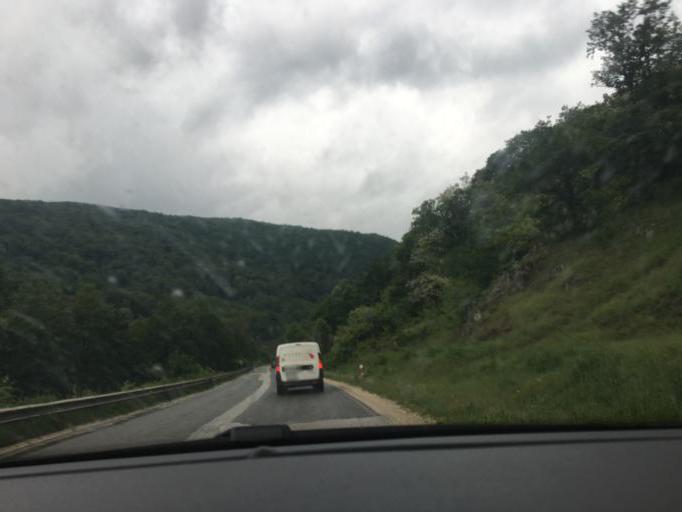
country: MK
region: Kicevo
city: Zajas
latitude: 41.6407
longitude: 20.8958
